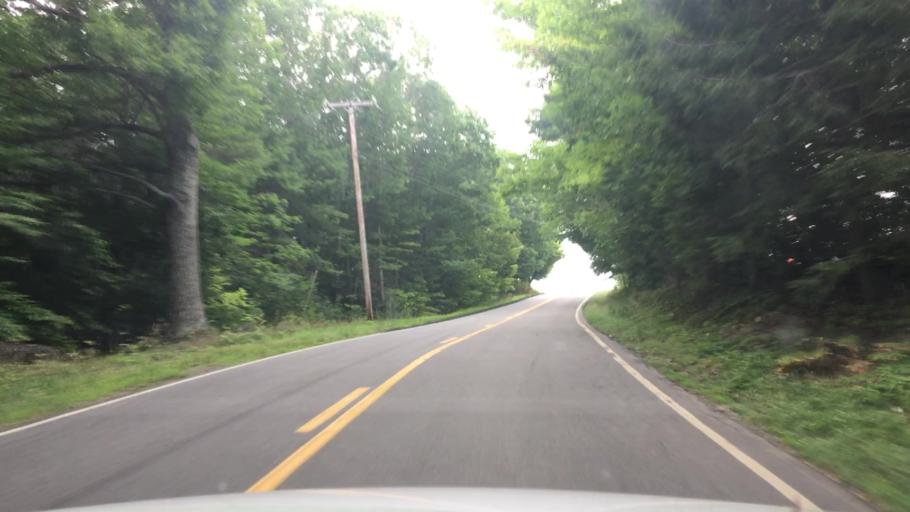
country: US
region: Maine
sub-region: Knox County
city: Washington
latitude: 44.2322
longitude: -69.3863
